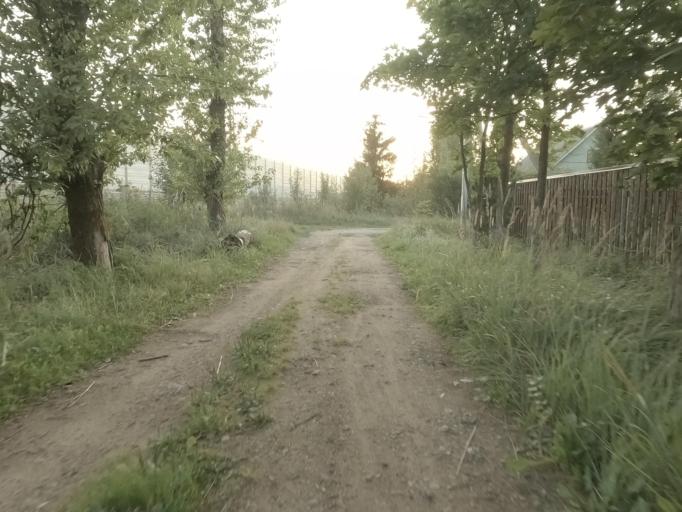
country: RU
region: Leningrad
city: Mga
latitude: 59.7581
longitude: 31.0430
